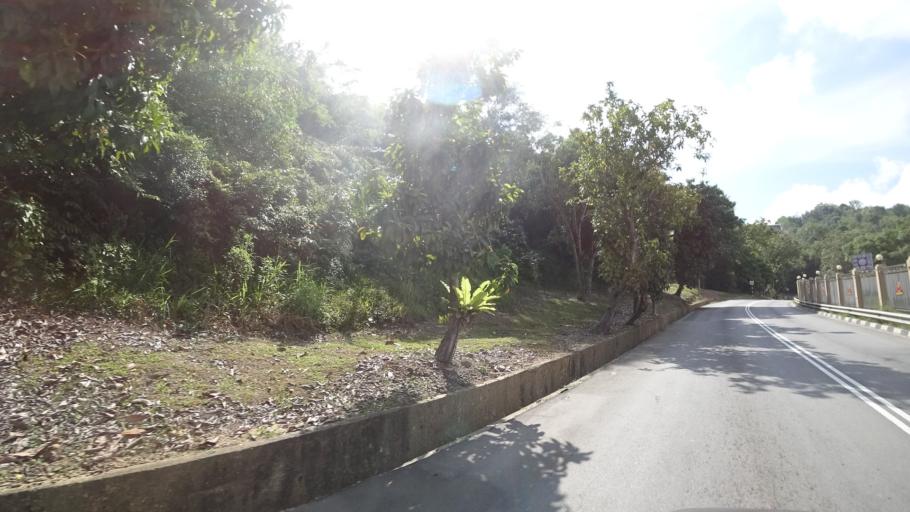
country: BN
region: Brunei and Muara
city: Bandar Seri Begawan
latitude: 4.8856
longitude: 114.9497
